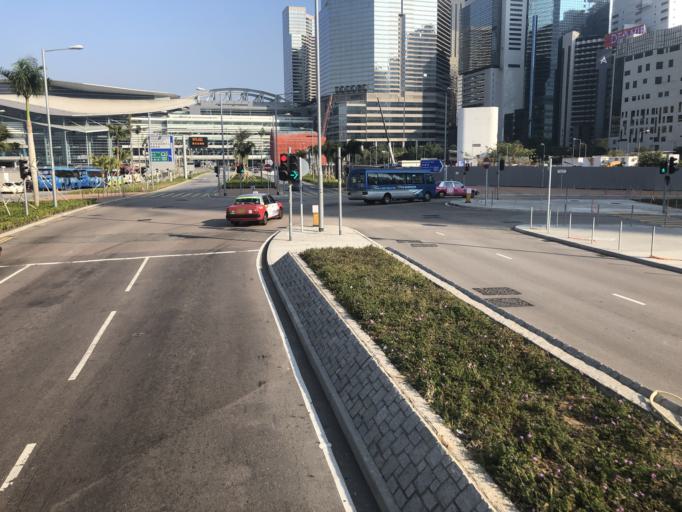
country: HK
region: Wanchai
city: Wan Chai
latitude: 22.2822
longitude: 114.1682
